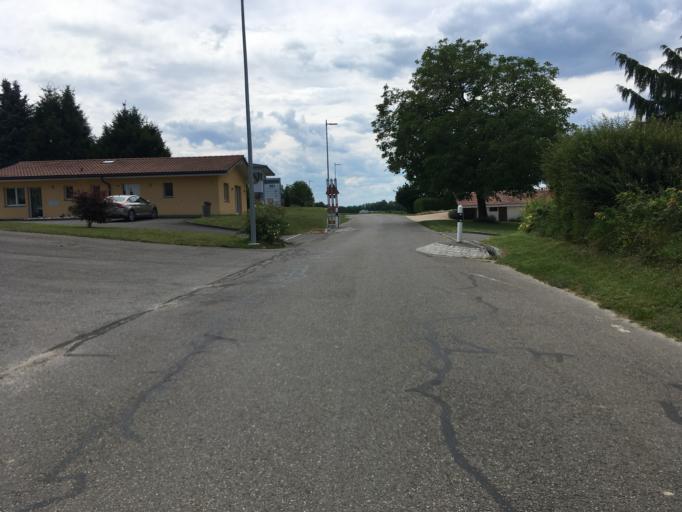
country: CH
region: Fribourg
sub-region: Broye District
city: Estavayer-le-Lac
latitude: 46.8729
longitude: 6.8846
